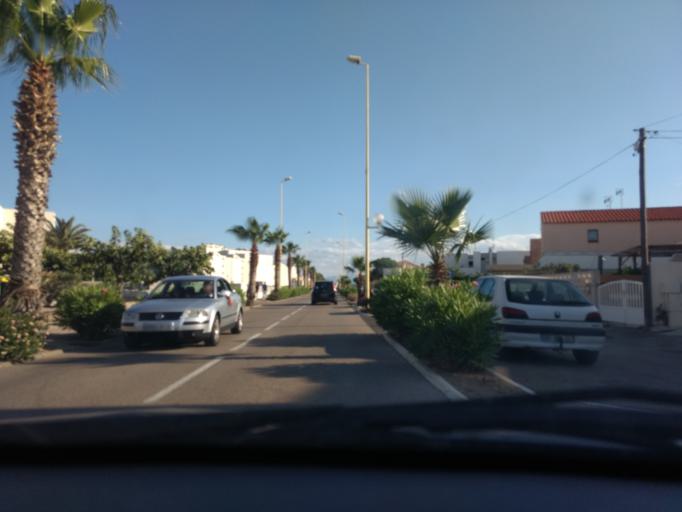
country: FR
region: Languedoc-Roussillon
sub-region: Departement des Pyrenees-Orientales
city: Le Barcares
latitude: 42.8035
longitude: 3.0372
